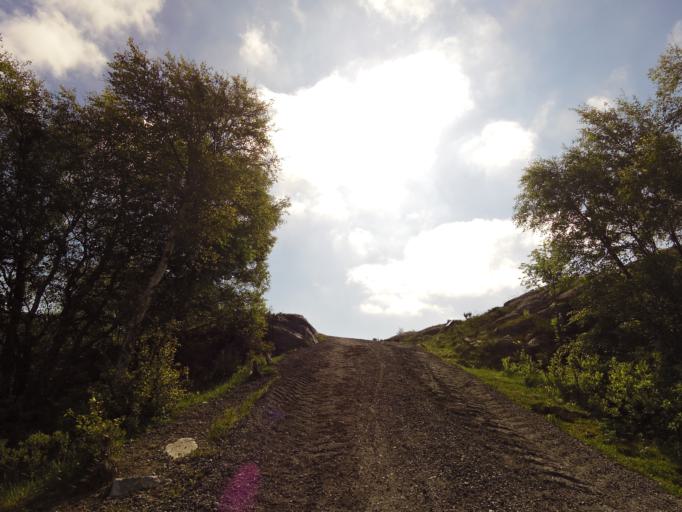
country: NO
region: Rogaland
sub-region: Ha
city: Vigrestad
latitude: 58.5144
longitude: 5.8304
